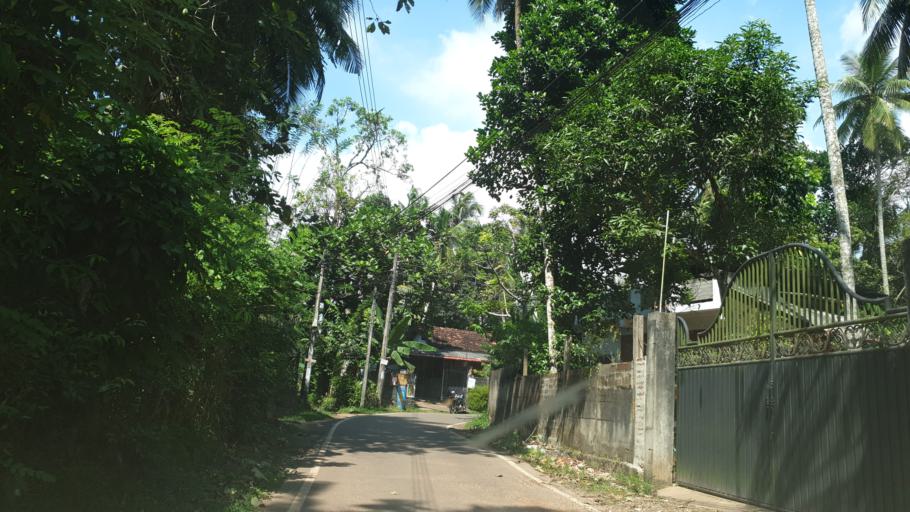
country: LK
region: Western
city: Panadura
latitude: 6.7104
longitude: 79.9593
